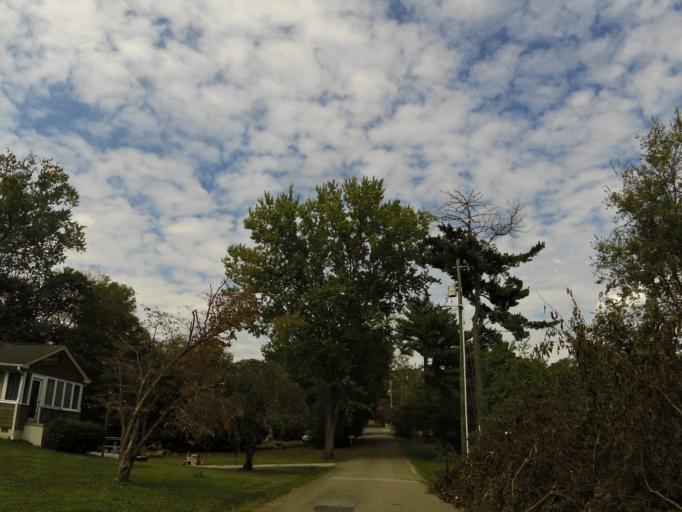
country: US
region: Tennessee
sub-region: Knox County
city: Mascot
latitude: 36.0020
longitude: -83.8280
